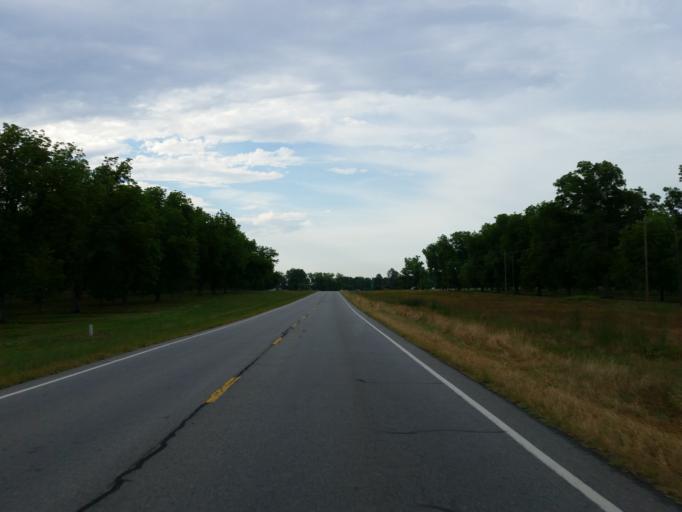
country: US
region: Georgia
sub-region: Dooly County
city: Vienna
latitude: 32.0428
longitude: -83.7951
